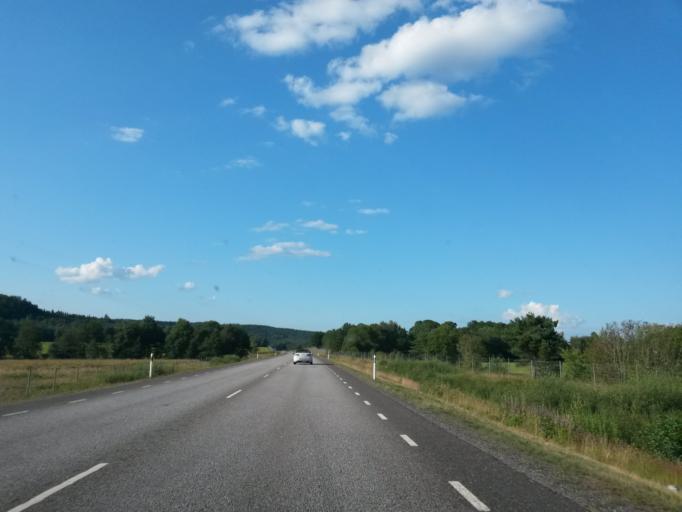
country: SE
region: Vaestra Goetaland
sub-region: Alingsas Kommun
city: Ingared
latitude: 57.9488
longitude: 12.3921
